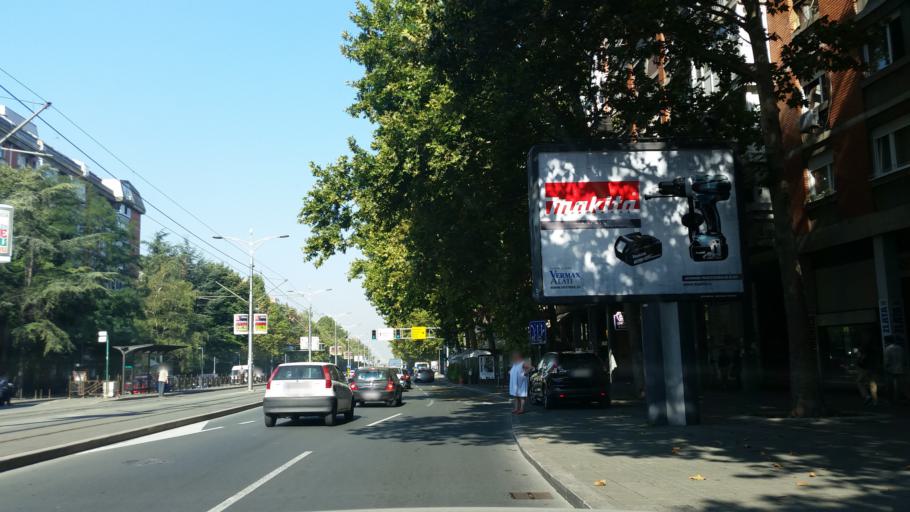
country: RS
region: Central Serbia
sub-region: Belgrade
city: Palilula
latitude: 44.7951
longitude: 20.5003
